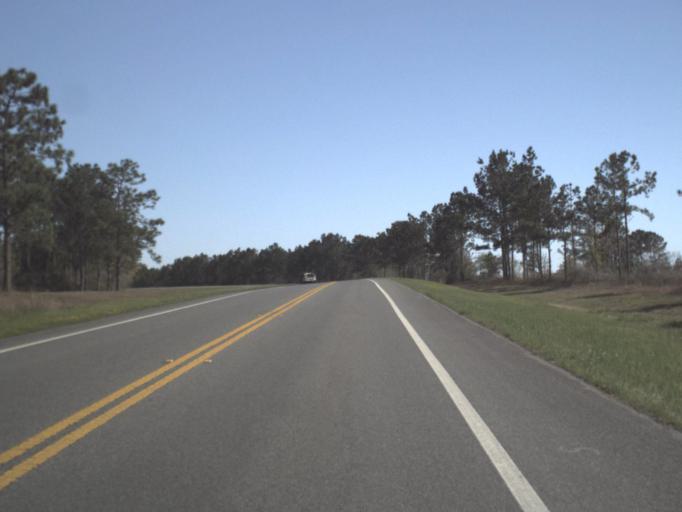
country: US
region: Florida
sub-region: Walton County
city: DeFuniak Springs
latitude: 30.7180
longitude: -86.0202
